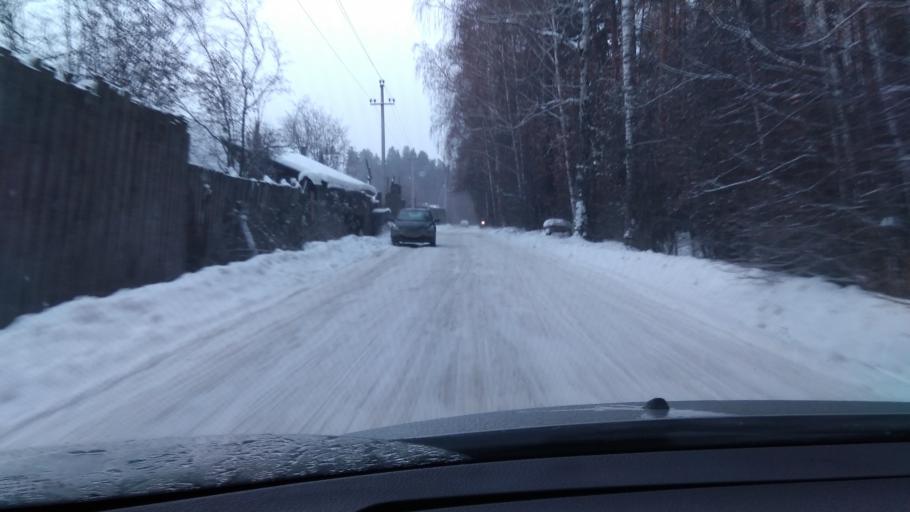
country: RU
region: Sverdlovsk
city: Verkhnyaya Pyshma
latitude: 56.9214
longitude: 60.5848
